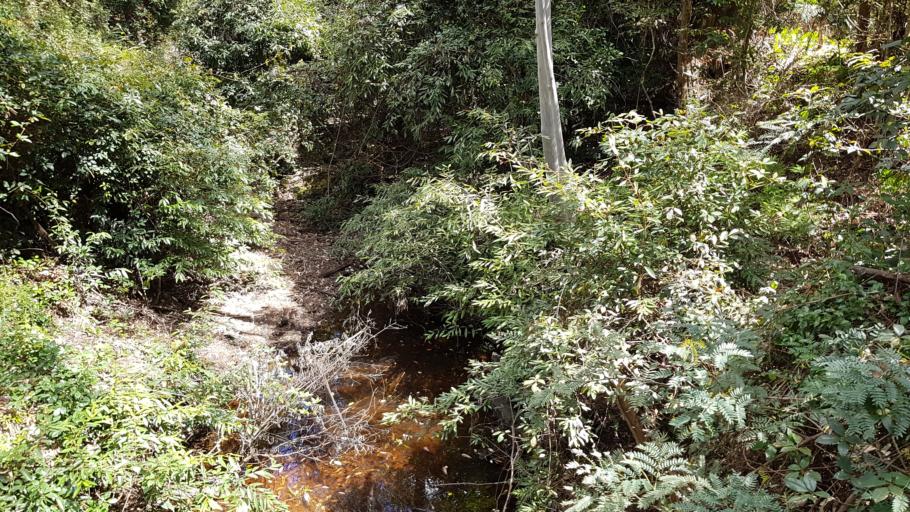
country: AU
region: New South Wales
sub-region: Hornsby Shire
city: Glenorie
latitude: -33.4004
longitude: 151.0488
